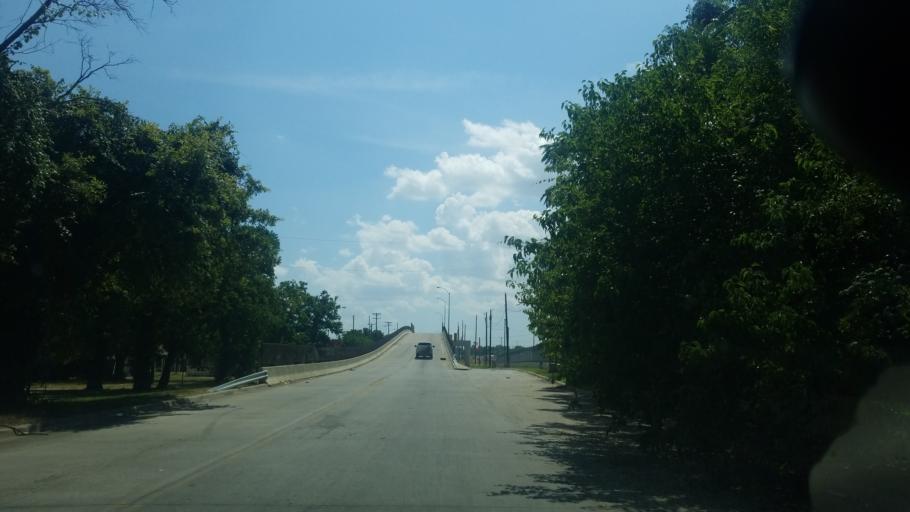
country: US
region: Texas
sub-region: Dallas County
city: Hutchins
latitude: 32.7185
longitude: -96.7495
